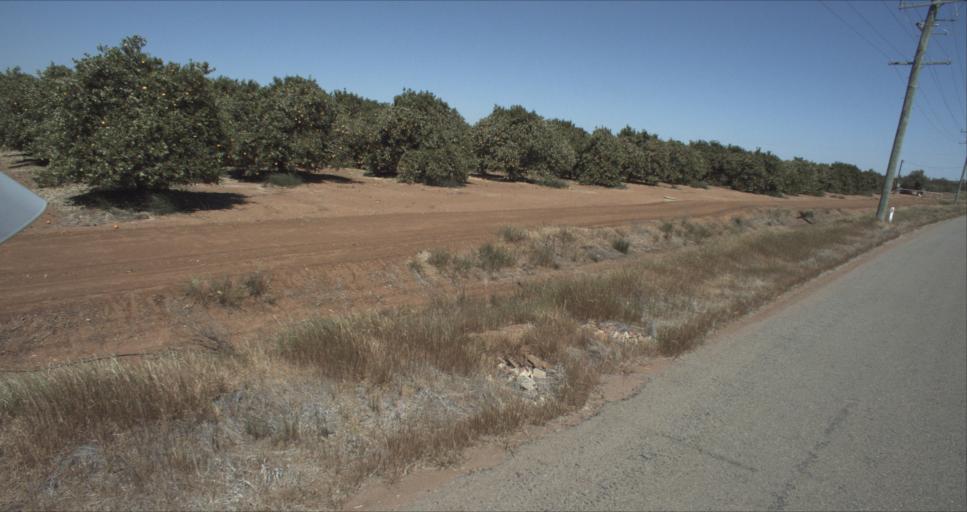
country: AU
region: New South Wales
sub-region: Leeton
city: Leeton
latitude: -34.4960
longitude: 146.4213
